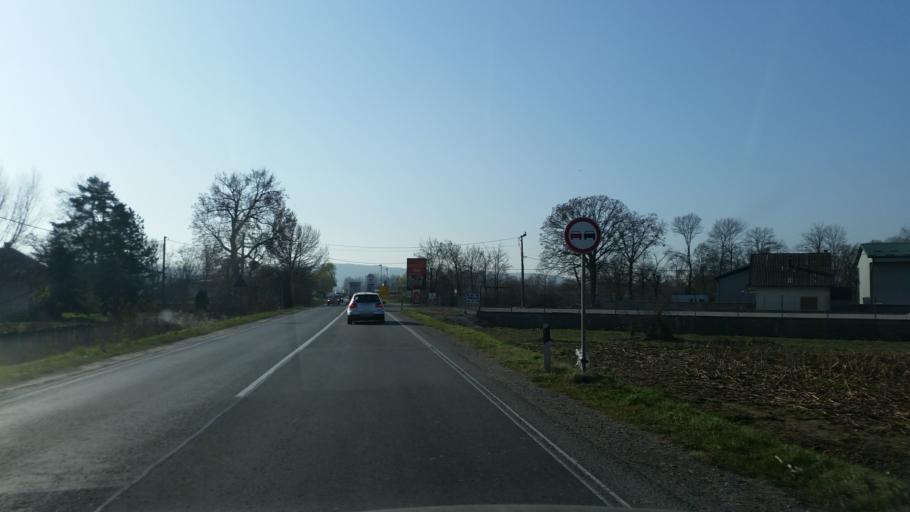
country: RS
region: Central Serbia
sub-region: Belgrade
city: Lazarevac
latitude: 44.3933
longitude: 20.2412
